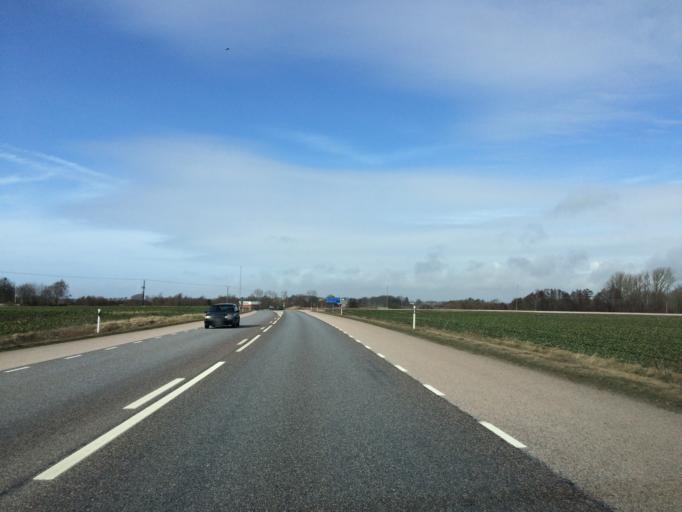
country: SE
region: Halland
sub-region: Laholms Kommun
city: Veinge
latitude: 56.5705
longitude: 13.0223
